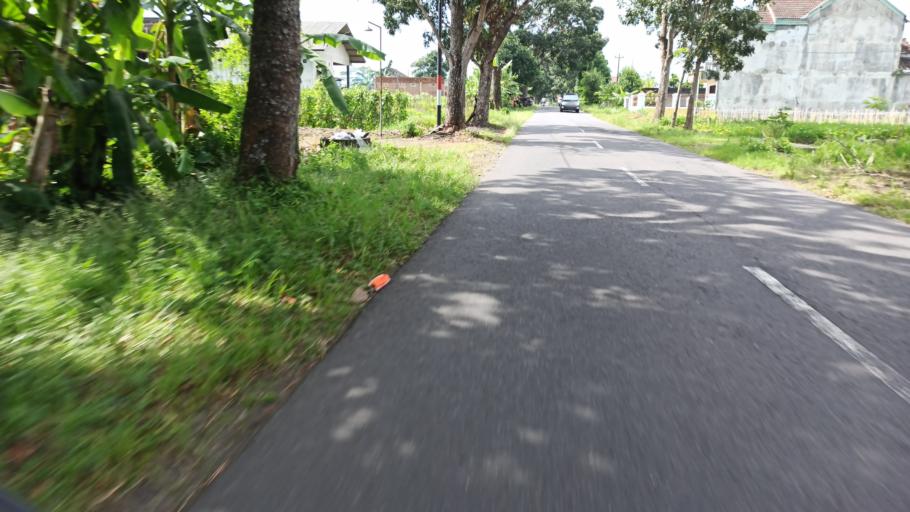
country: ID
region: Daerah Istimewa Yogyakarta
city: Sleman
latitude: -7.6928
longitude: 110.2939
